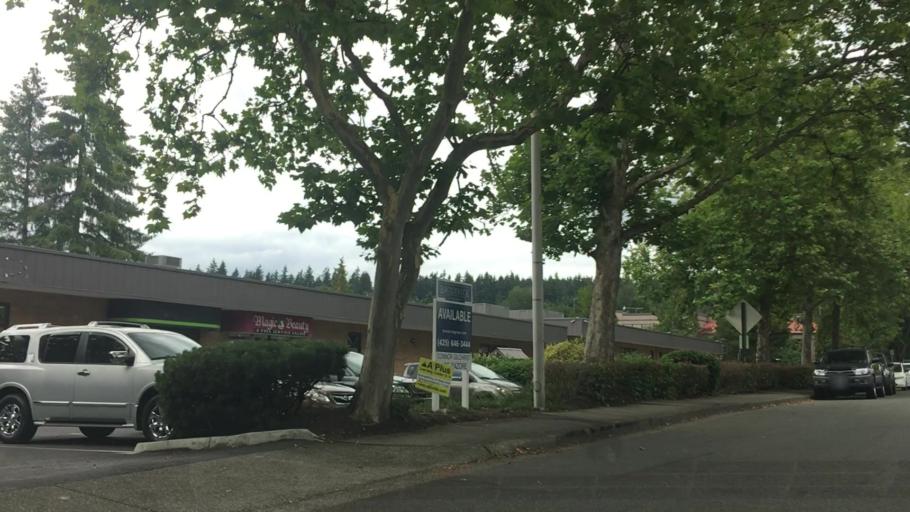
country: US
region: Washington
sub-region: King County
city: Bellevue
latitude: 47.6263
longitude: -122.1645
